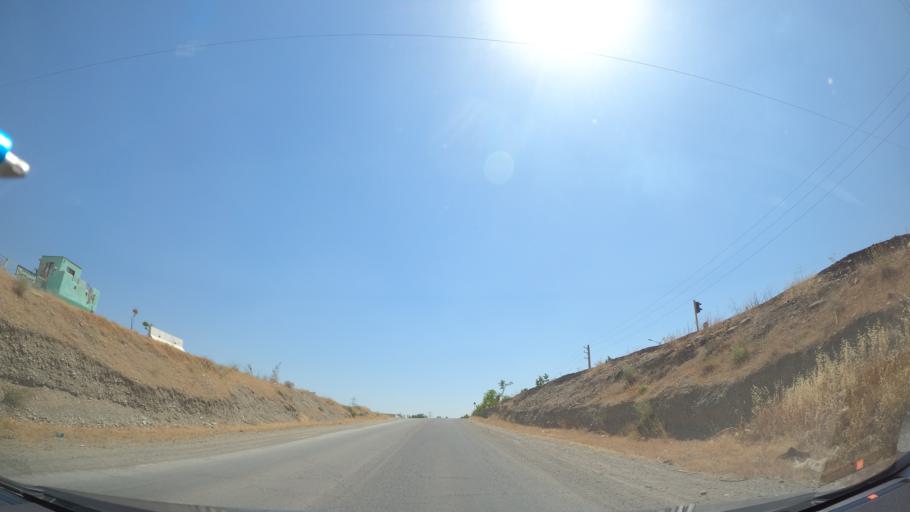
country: IR
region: Alborz
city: Hashtgerd
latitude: 35.9153
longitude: 50.7333
